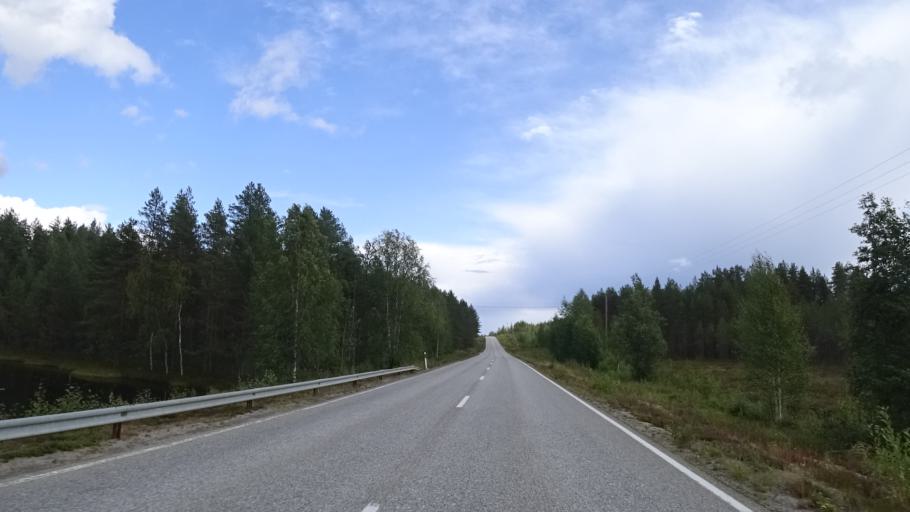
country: FI
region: North Karelia
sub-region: Joensuu
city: Ilomantsi
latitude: 62.6430
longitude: 31.0492
